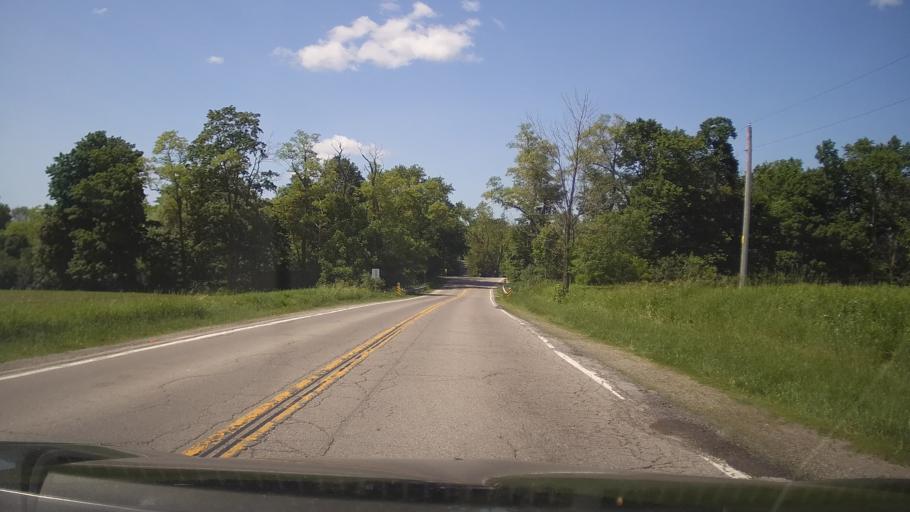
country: CA
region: Ontario
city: Oshawa
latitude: 43.9919
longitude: -78.8617
